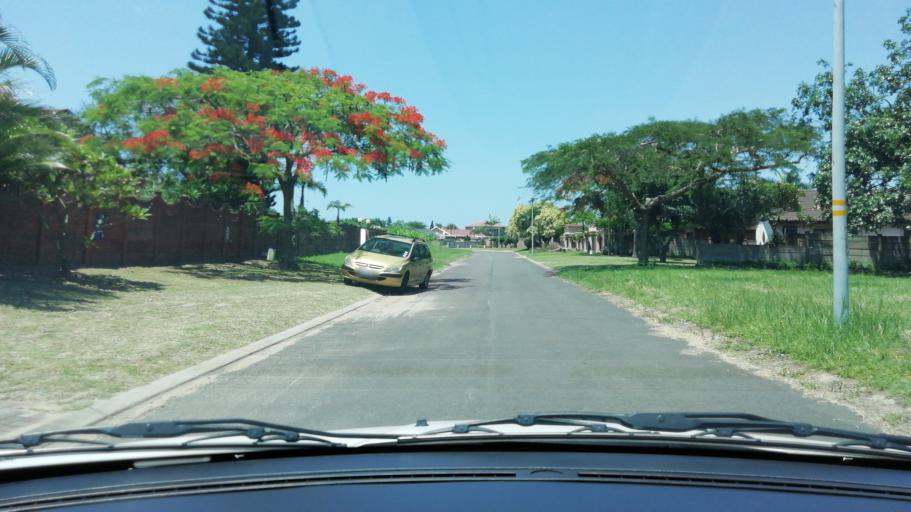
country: ZA
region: KwaZulu-Natal
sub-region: uThungulu District Municipality
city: Richards Bay
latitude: -28.7333
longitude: 32.0525
